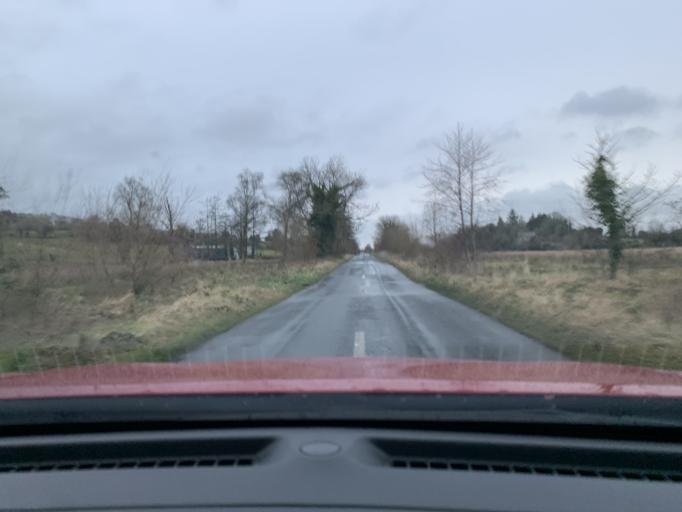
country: IE
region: Connaught
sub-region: Roscommon
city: Boyle
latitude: 54.0321
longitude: -8.3351
